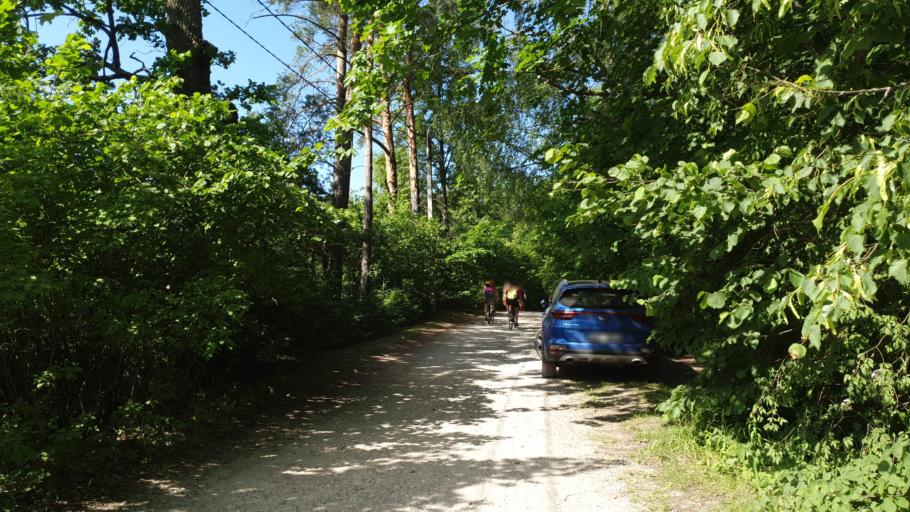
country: LT
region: Vilnius County
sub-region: Vilnius
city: Fabijoniskes
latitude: 54.7839
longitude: 25.3274
